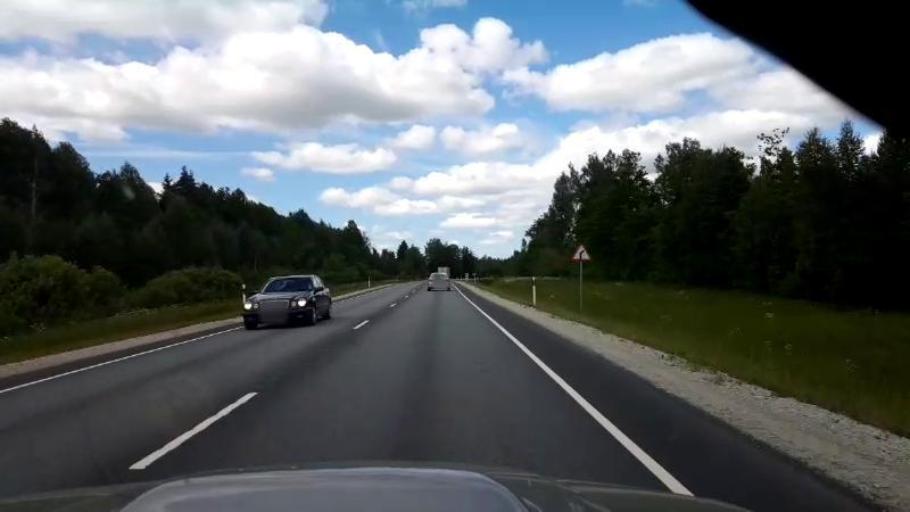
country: EE
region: Paernumaa
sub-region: Halinga vald
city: Parnu-Jaagupi
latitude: 58.6745
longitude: 24.4431
